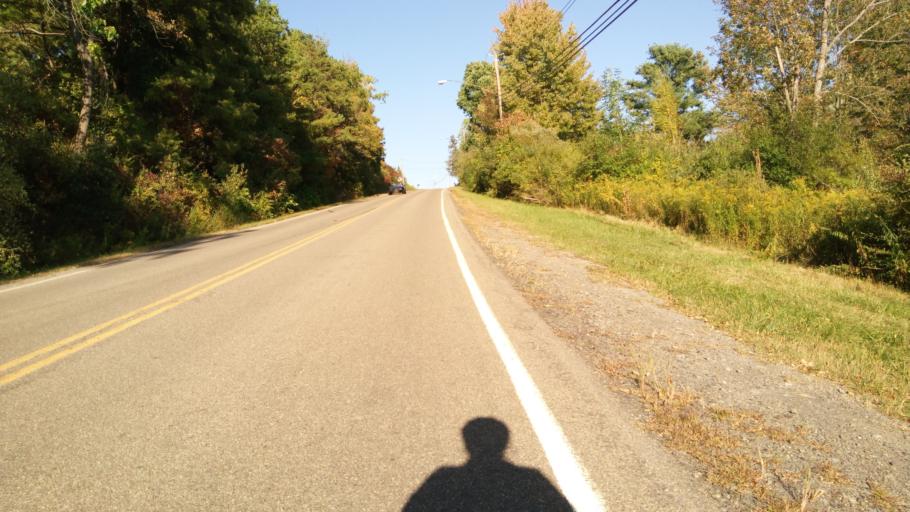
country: US
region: New York
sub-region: Chemung County
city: West Elmira
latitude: 42.0692
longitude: -76.8346
